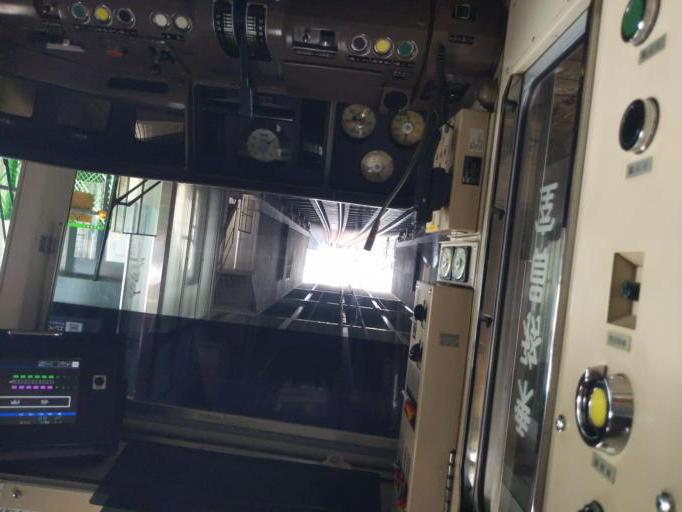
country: JP
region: Kanagawa
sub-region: Kawasaki-shi
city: Kawasaki
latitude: 35.5642
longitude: 139.6540
